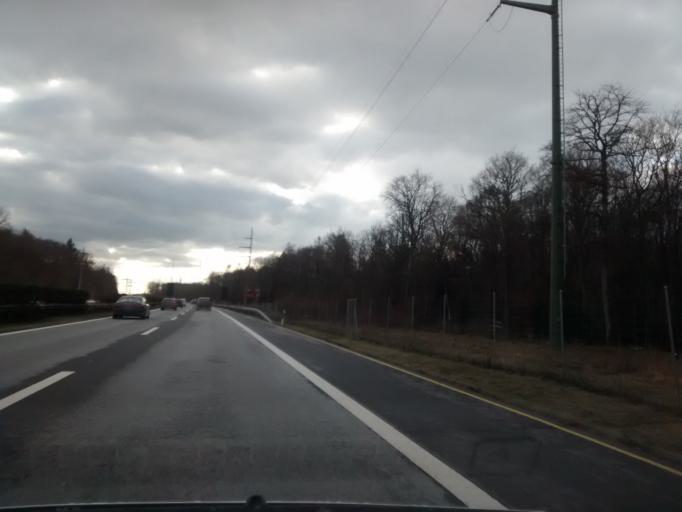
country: CH
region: Vaud
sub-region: Nyon District
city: Founex
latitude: 46.3569
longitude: 6.1787
